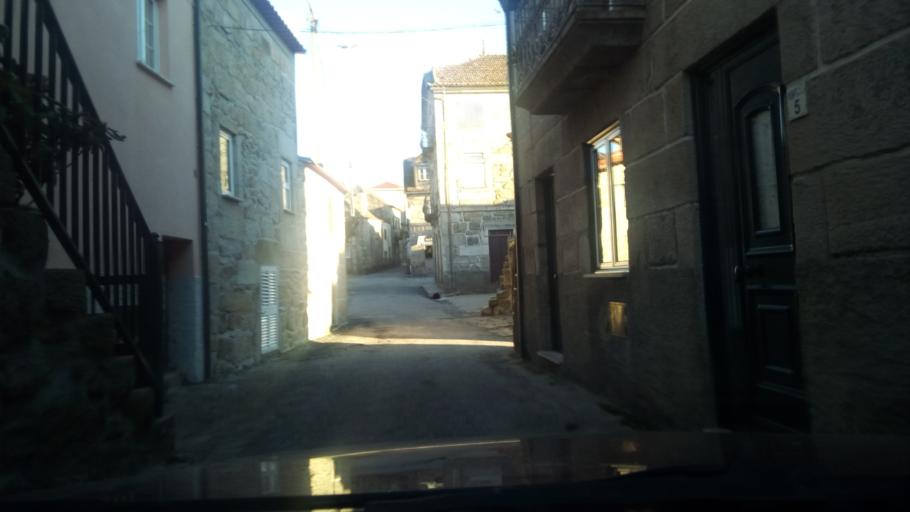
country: PT
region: Guarda
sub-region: Fornos de Algodres
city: Fornos de Algodres
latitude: 40.6096
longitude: -7.5081
